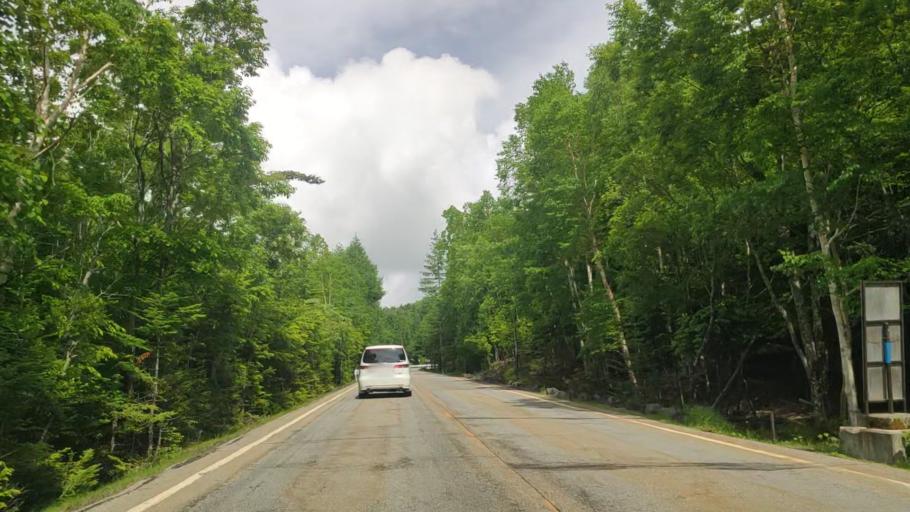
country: JP
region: Yamanashi
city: Fujikawaguchiko
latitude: 35.4063
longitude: 138.7001
